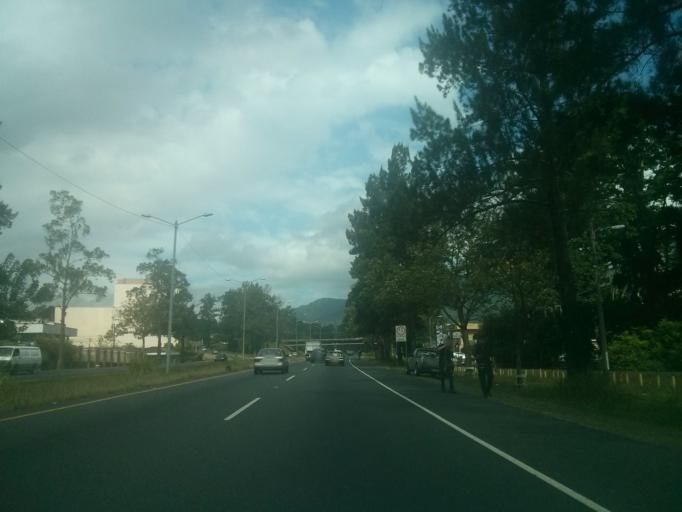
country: CR
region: San Jose
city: Curridabat
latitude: 9.9107
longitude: -84.0201
